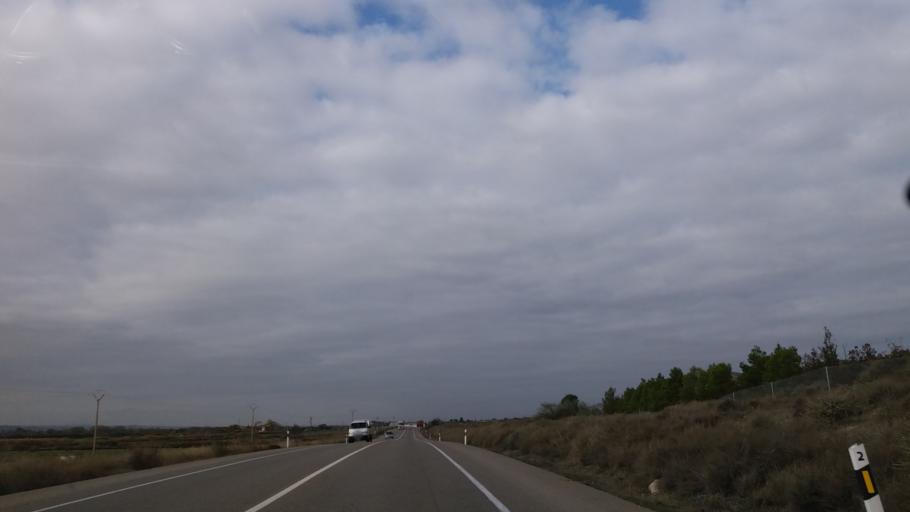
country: ES
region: Aragon
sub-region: Provincia de Zaragoza
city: Villafranca de Ebro
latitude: 41.5592
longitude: -0.6167
